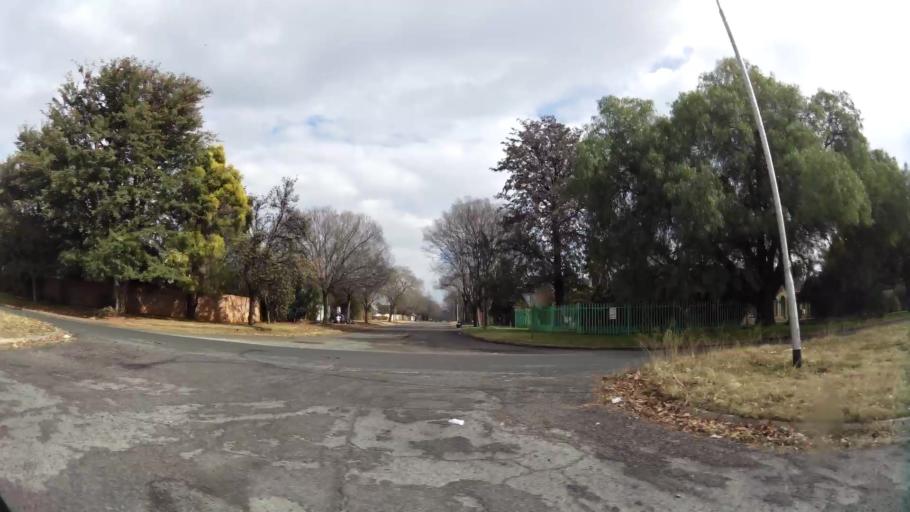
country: ZA
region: Gauteng
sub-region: Sedibeng District Municipality
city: Vanderbijlpark
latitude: -26.7264
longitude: 27.8628
